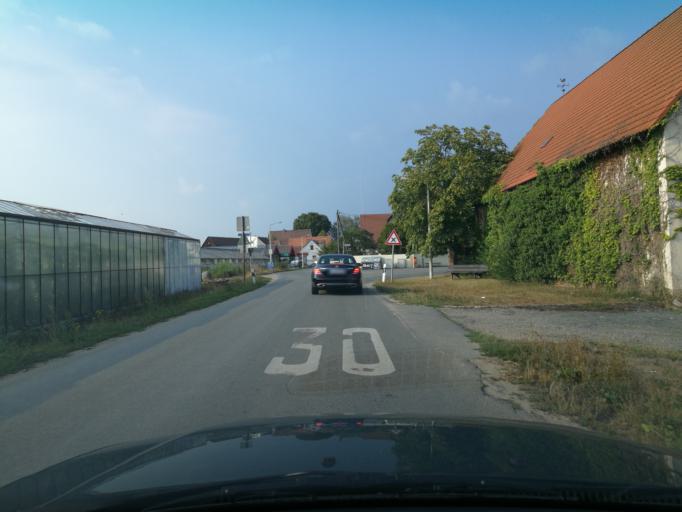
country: DE
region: Bavaria
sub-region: Regierungsbezirk Mittelfranken
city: Nuernberg
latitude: 49.4854
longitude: 11.0724
